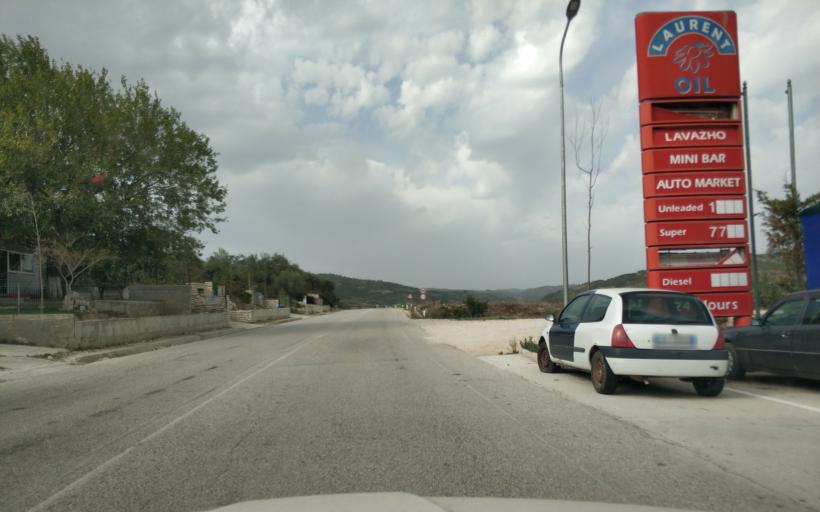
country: AL
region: Gjirokaster
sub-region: Rrethi i Tepelenes
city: Krahes
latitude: 40.4327
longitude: 19.8520
